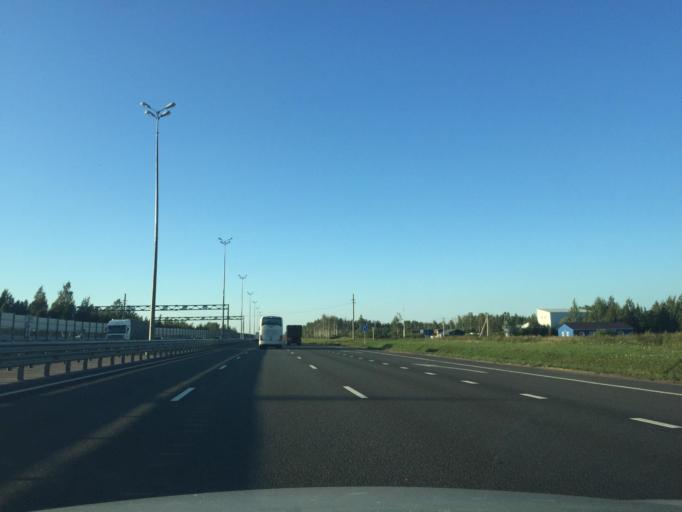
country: RU
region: Leningrad
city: Gatchina
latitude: 59.5611
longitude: 30.1665
